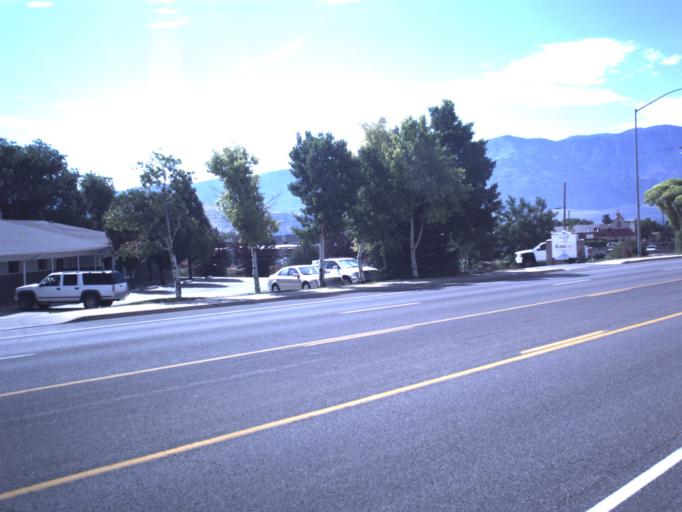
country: US
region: Utah
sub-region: Sevier County
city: Richfield
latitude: 38.7799
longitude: -112.0849
